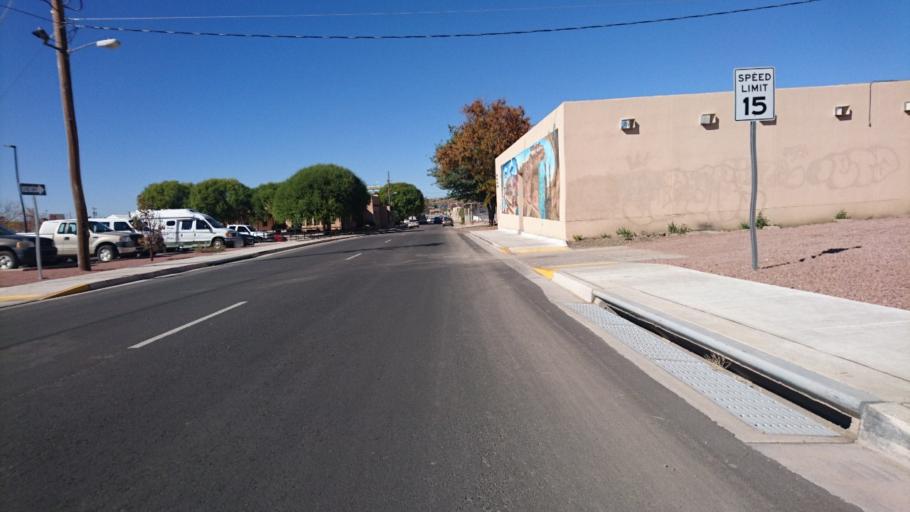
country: US
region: New Mexico
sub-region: McKinley County
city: Gallup
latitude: 35.5248
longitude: -108.7413
